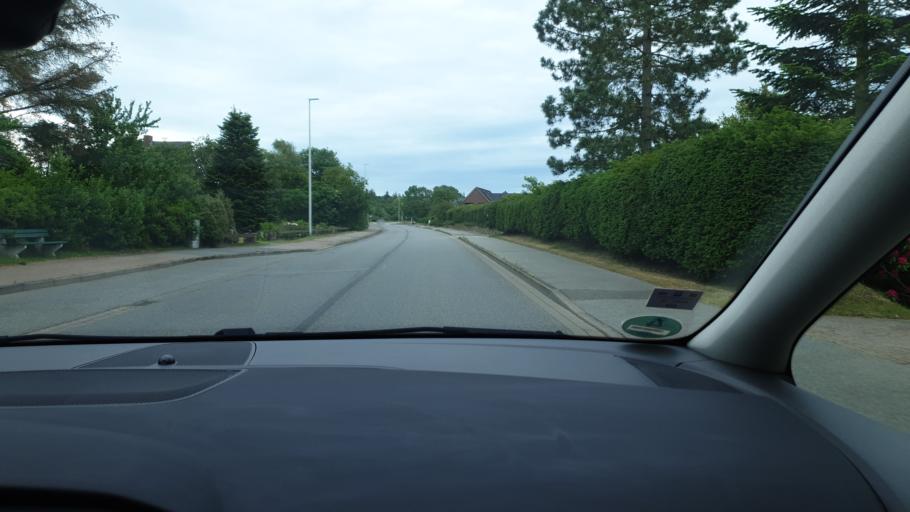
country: DE
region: Schleswig-Holstein
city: Schobull
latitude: 54.5130
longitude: 8.9981
